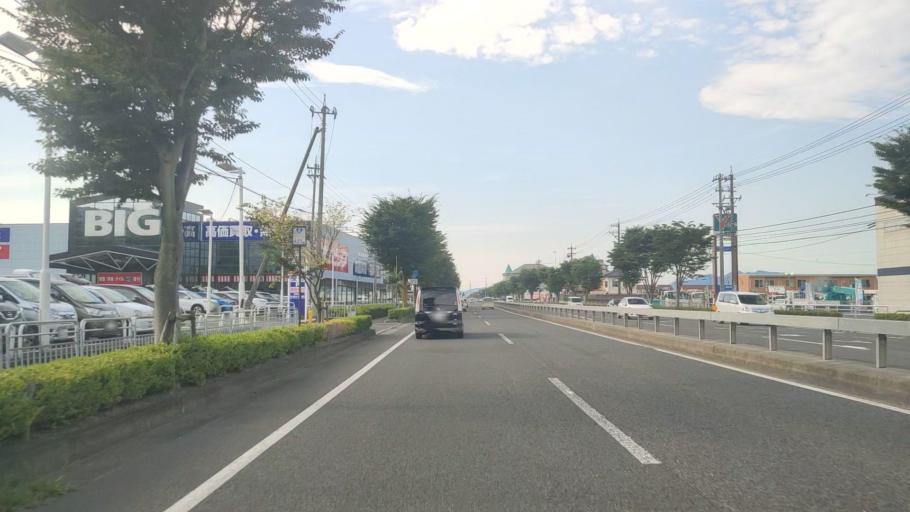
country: JP
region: Fukui
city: Takefu
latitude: 35.9126
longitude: 136.1916
